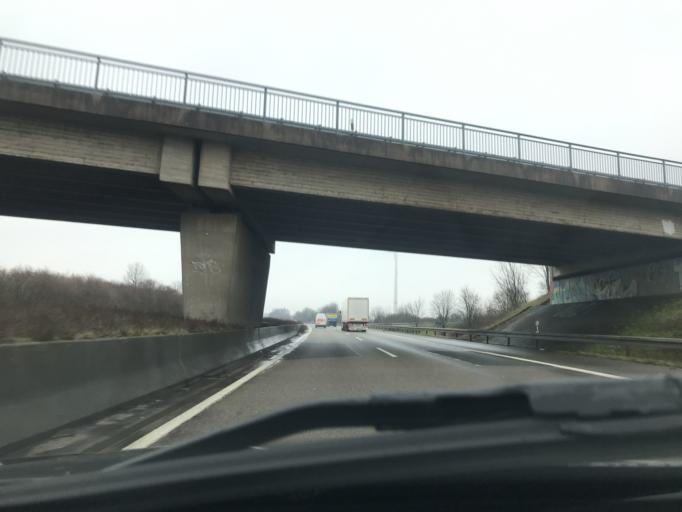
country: DE
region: North Rhine-Westphalia
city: Rheinberg
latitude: 51.5124
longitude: 6.5845
